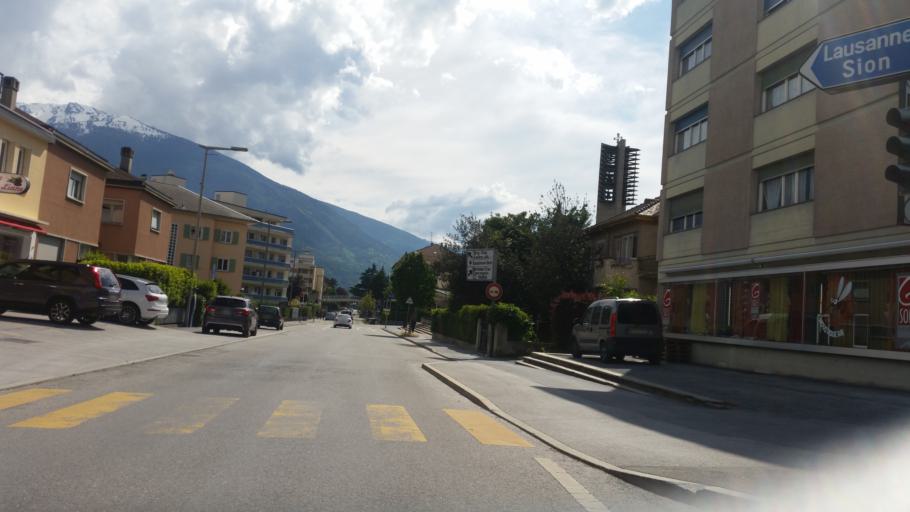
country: CH
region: Valais
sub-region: Sierre District
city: Sierre
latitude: 46.2924
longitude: 7.5259
